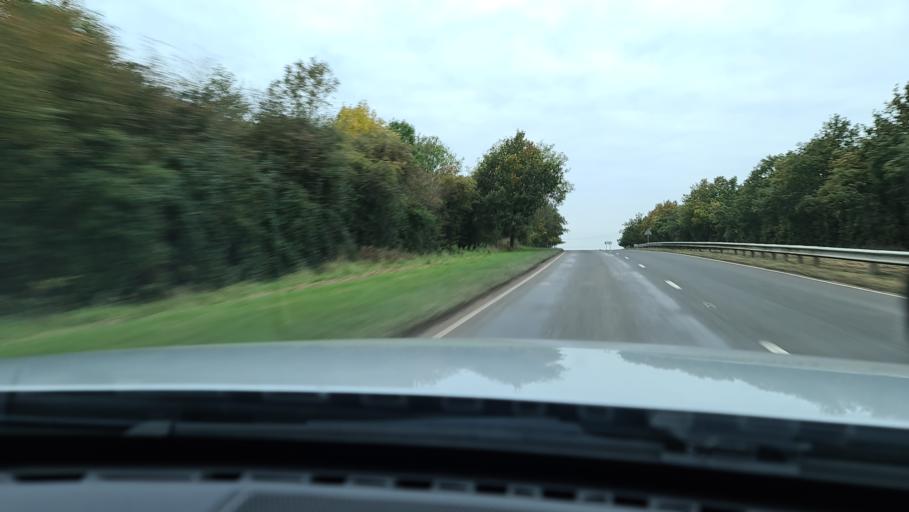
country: GB
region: England
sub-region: Buckinghamshire
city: Steeple Claydon
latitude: 51.8687
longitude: -1.0088
